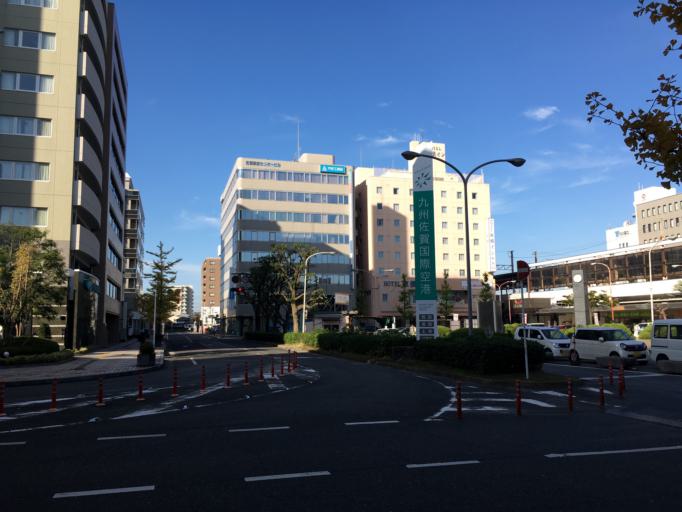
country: JP
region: Saga Prefecture
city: Saga-shi
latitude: 33.2636
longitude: 130.2980
